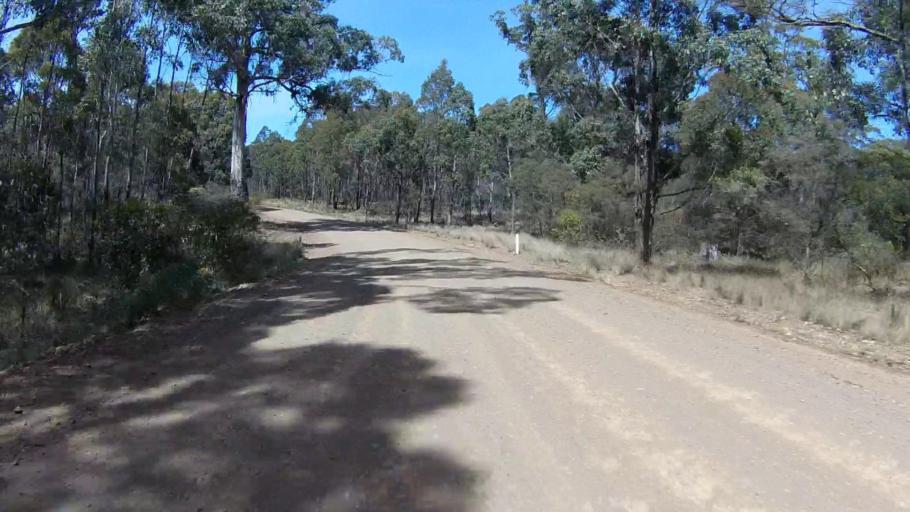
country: AU
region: Tasmania
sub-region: Sorell
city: Sorell
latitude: -42.6648
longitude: 147.7298
